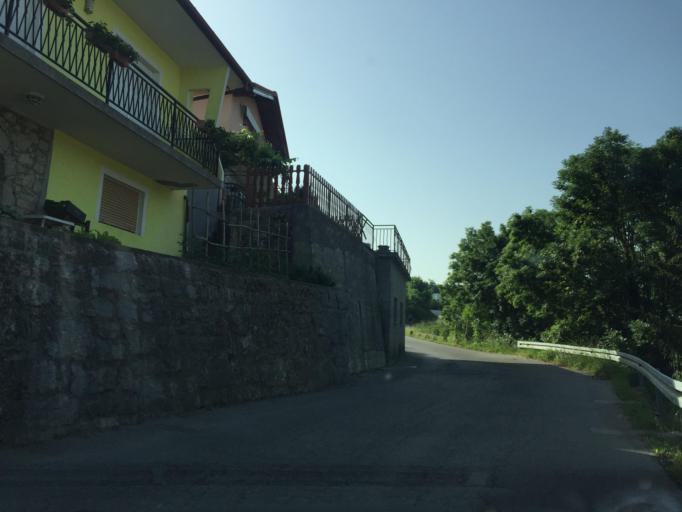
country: HR
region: Primorsko-Goranska
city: Kastav
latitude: 45.4192
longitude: 14.3123
